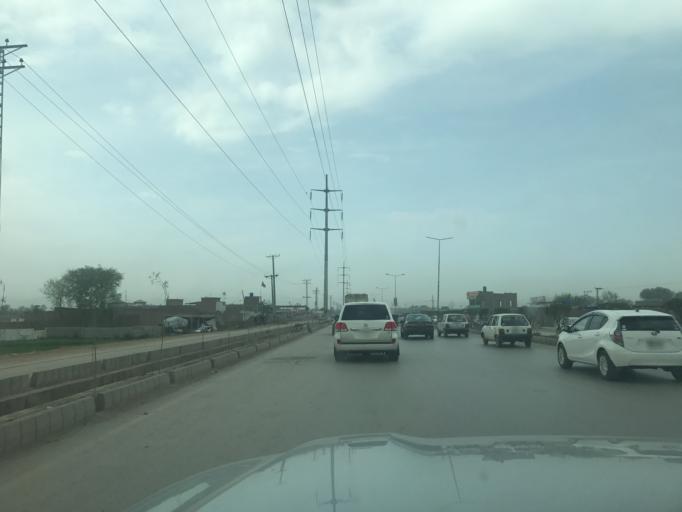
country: PK
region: Khyber Pakhtunkhwa
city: Peshawar
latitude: 33.9732
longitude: 71.5452
